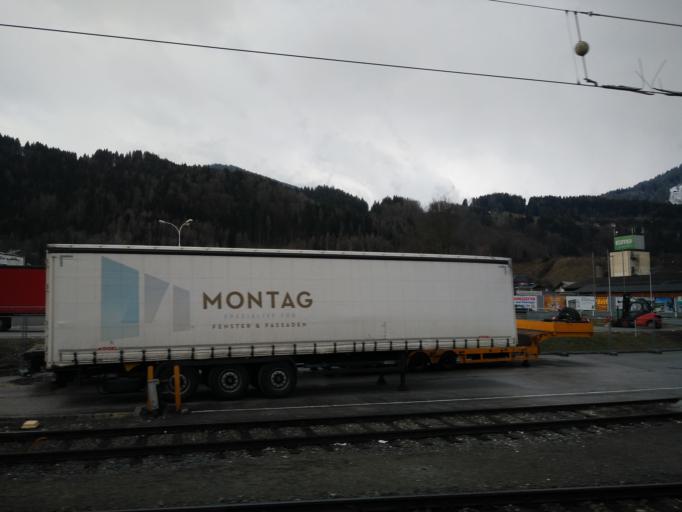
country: AT
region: Salzburg
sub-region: Politischer Bezirk Sankt Johann im Pongau
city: Bischofshofen
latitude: 47.4093
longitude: 13.2179
